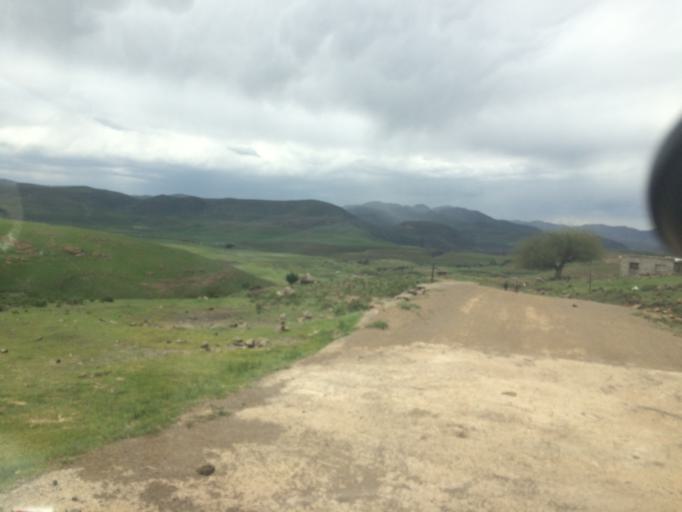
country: LS
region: Maseru
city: Nako
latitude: -29.8533
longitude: 28.0301
